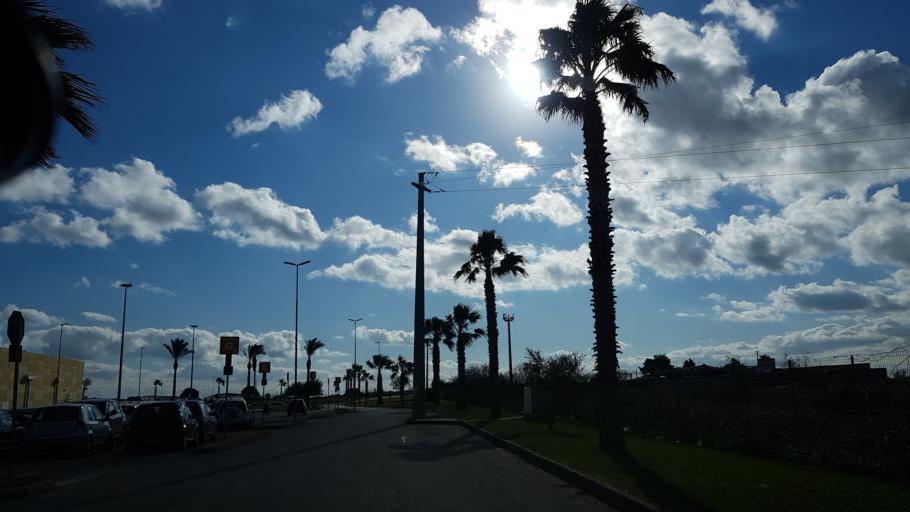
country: IT
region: Apulia
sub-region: Provincia di Brindisi
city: Brindisi
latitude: 40.6182
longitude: 17.9005
